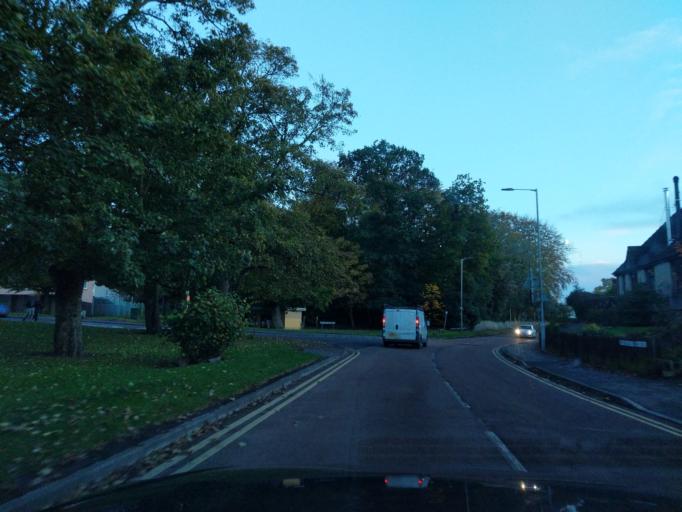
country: GB
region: Scotland
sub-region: Fife
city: Leuchars
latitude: 56.3810
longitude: -2.8820
